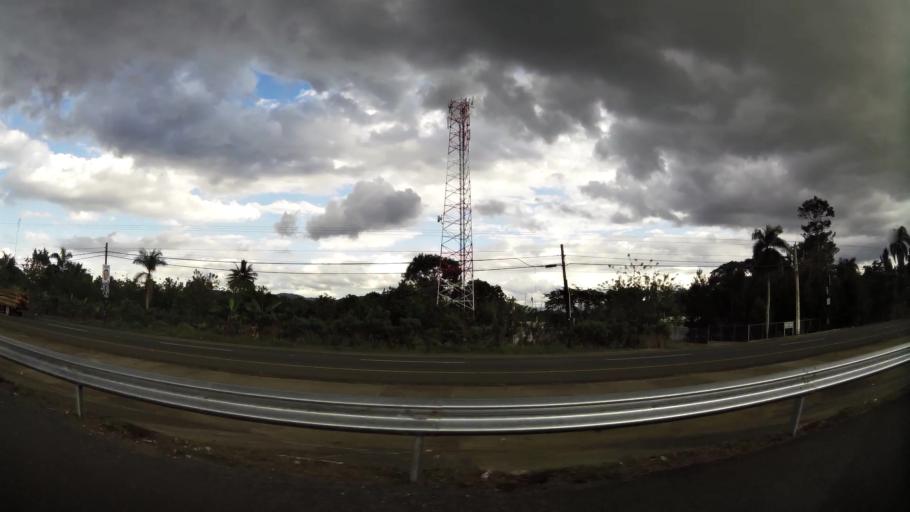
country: DO
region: Monsenor Nouel
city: Sabana del Puerto
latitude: 19.0218
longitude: -70.4458
